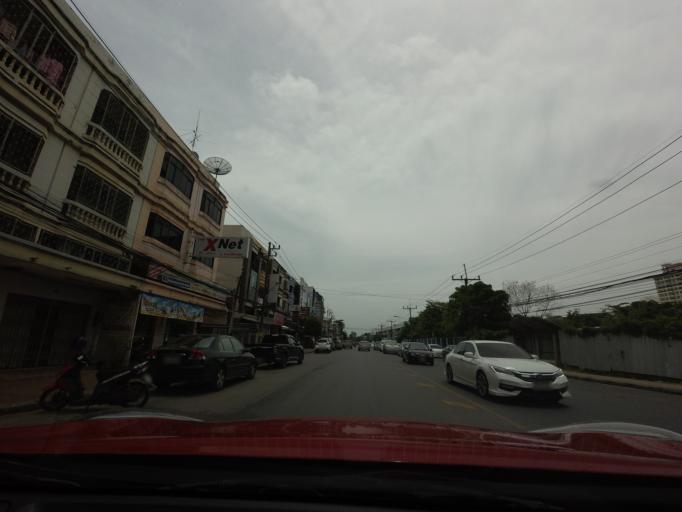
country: TH
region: Songkhla
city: Hat Yai
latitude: 7.0019
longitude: 100.4983
